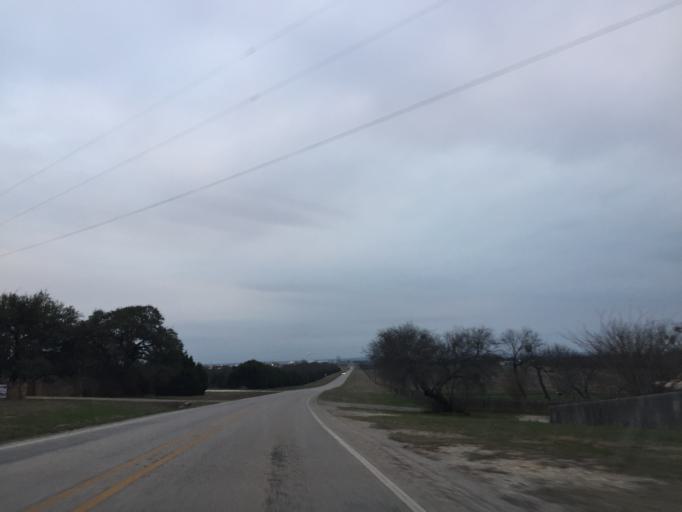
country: US
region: Texas
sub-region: Coryell County
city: Ames
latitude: 31.4988
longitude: -97.7280
